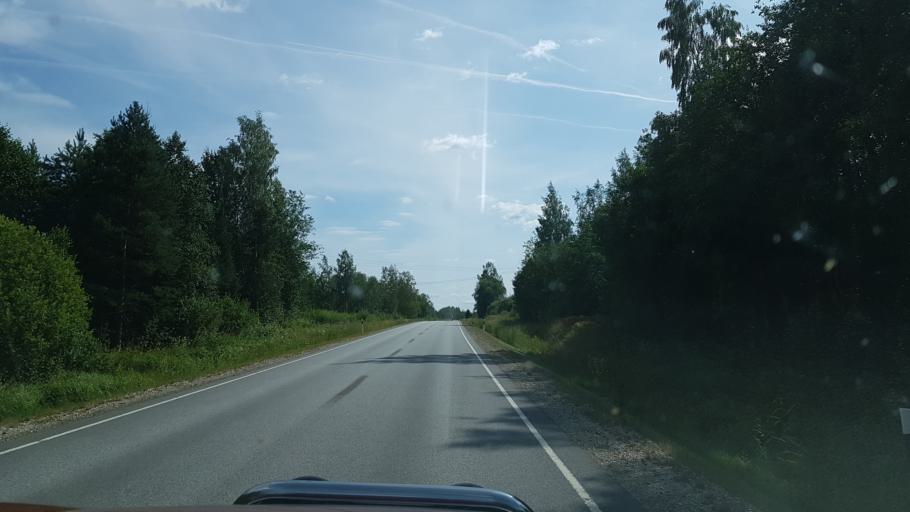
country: EE
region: Jogevamaa
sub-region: Mustvee linn
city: Mustvee
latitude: 58.9365
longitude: 26.8189
